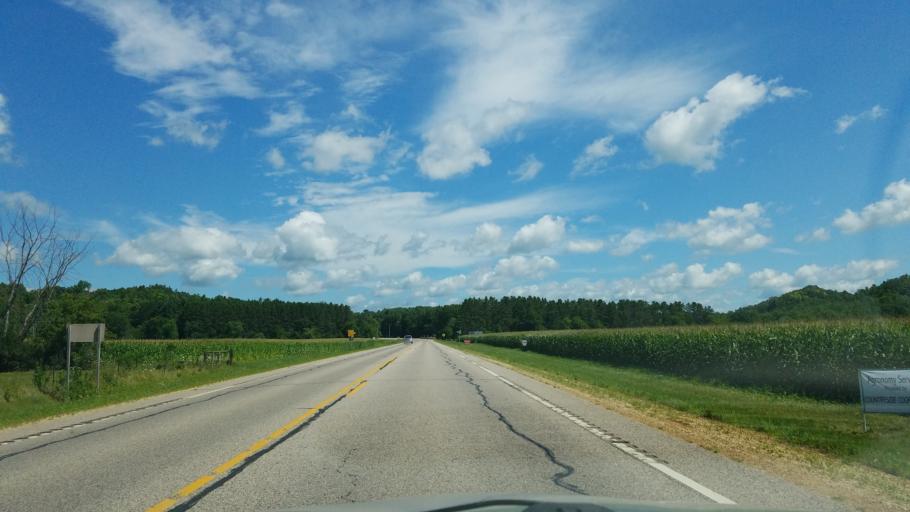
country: US
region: Wisconsin
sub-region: Saint Croix County
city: Glenwood City
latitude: 45.0404
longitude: -92.1764
